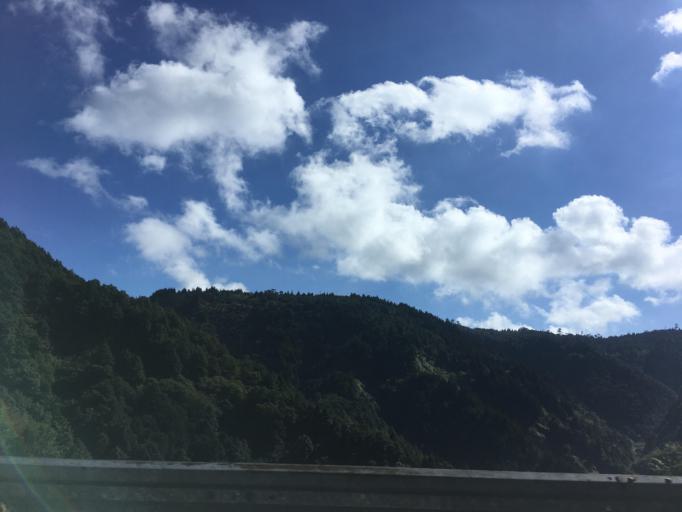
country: TW
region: Taiwan
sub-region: Yilan
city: Yilan
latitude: 24.5142
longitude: 121.5705
